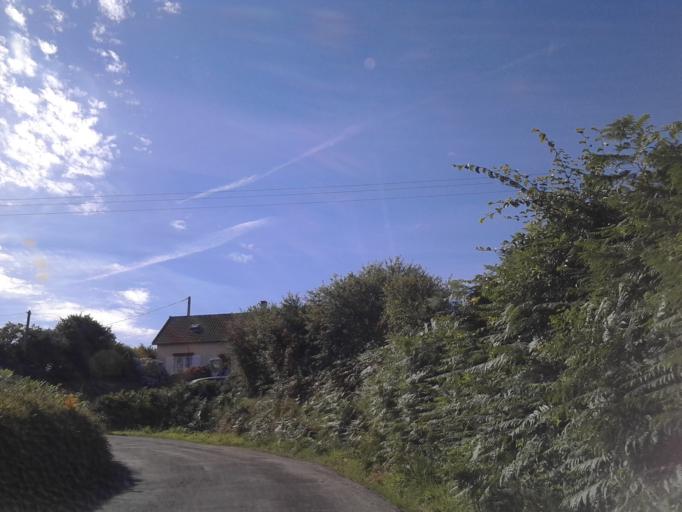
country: FR
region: Lower Normandy
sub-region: Departement de la Manche
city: Fermanville
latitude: 49.6856
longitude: -1.4589
